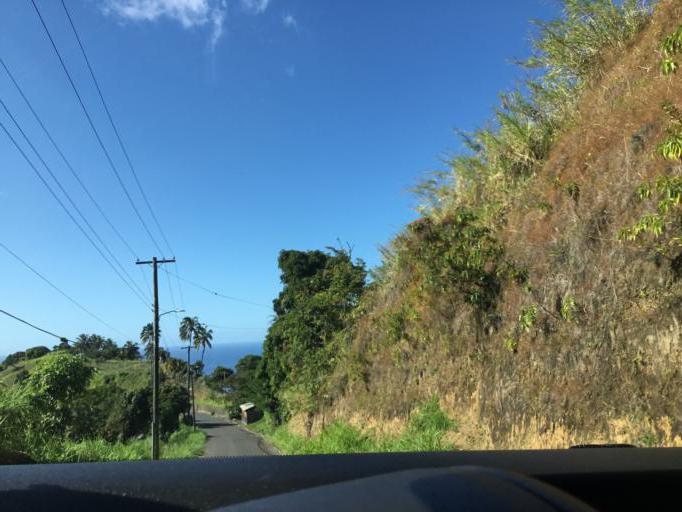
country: VC
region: Saint David
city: Chateaubelair
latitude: 13.2737
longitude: -61.2438
